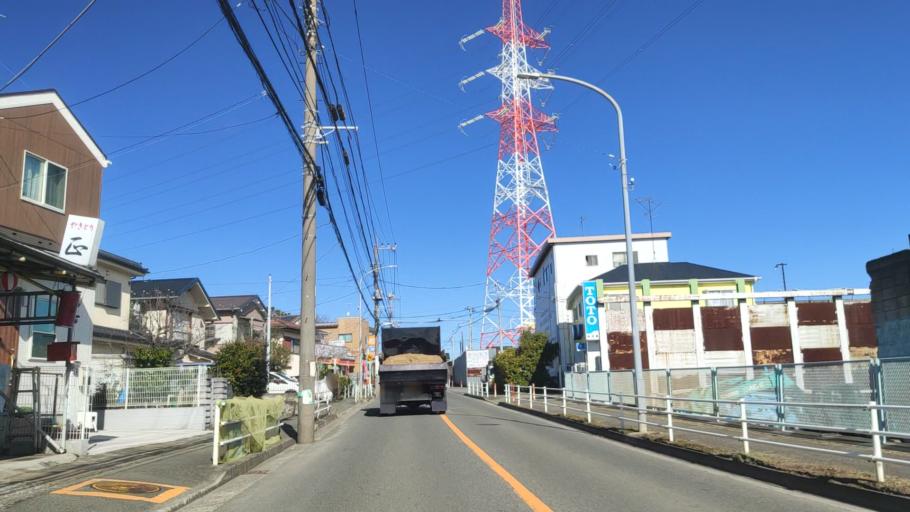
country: JP
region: Kanagawa
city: Minami-rinkan
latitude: 35.4916
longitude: 139.5165
